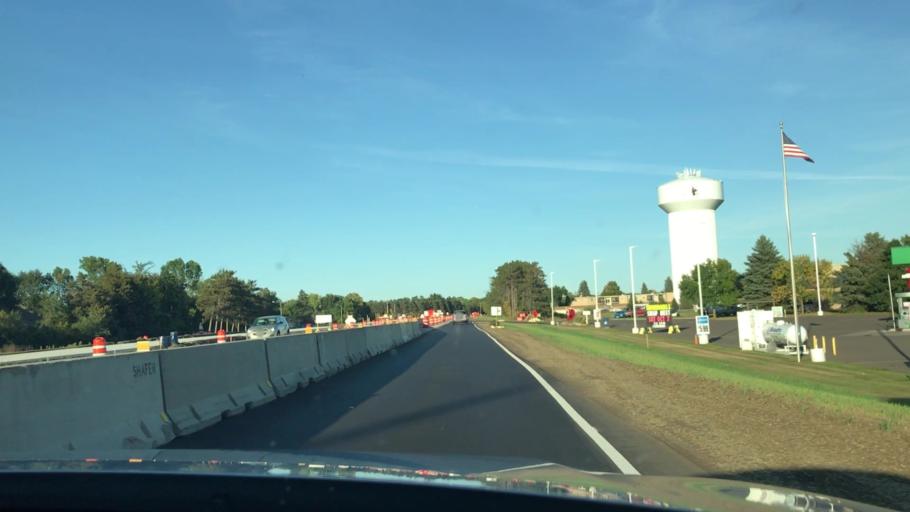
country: US
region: Minnesota
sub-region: Wright County
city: Otsego
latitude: 45.3069
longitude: -93.6081
